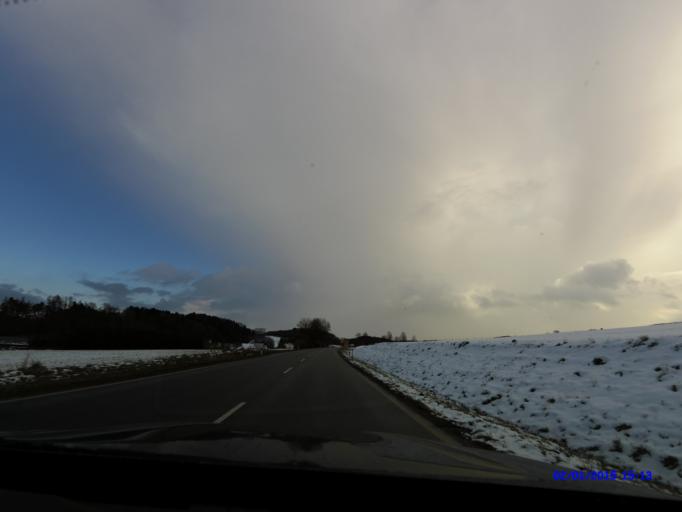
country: DE
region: Bavaria
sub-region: Lower Bavaria
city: Mainburg
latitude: 48.6236
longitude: 11.8069
